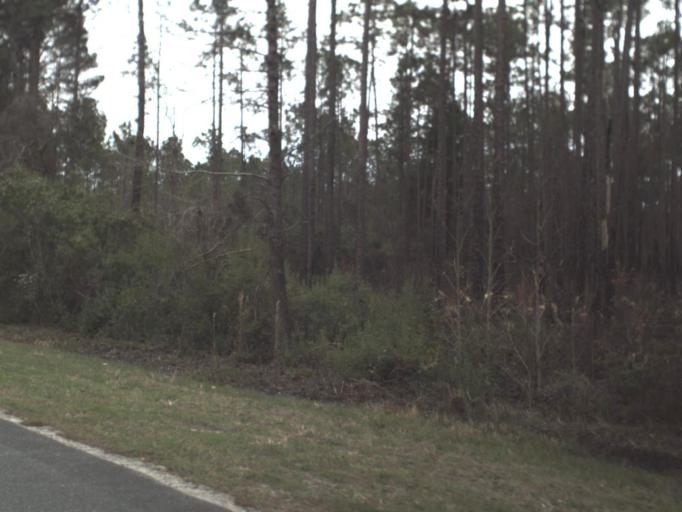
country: US
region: Florida
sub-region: Gadsden County
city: Midway
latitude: 30.3580
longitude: -84.5293
